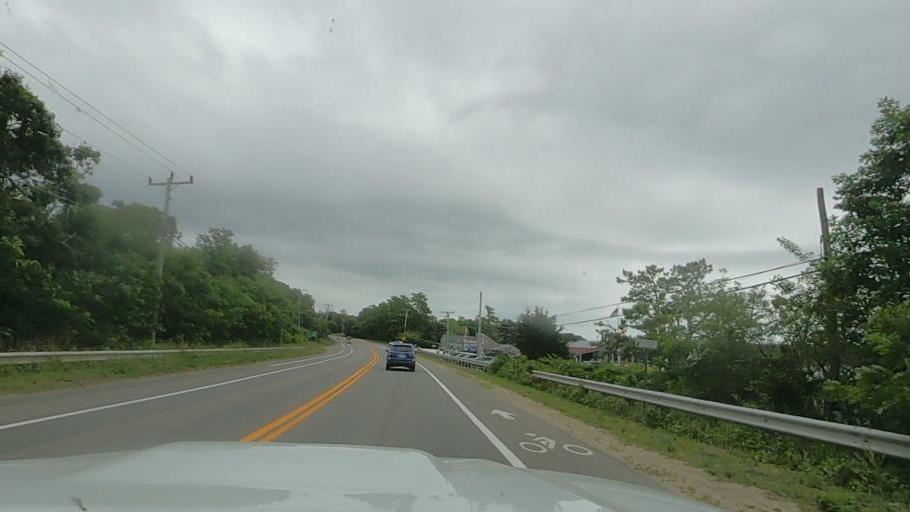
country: US
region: Massachusetts
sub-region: Barnstable County
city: Wellfleet
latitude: 41.9478
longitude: -70.0342
